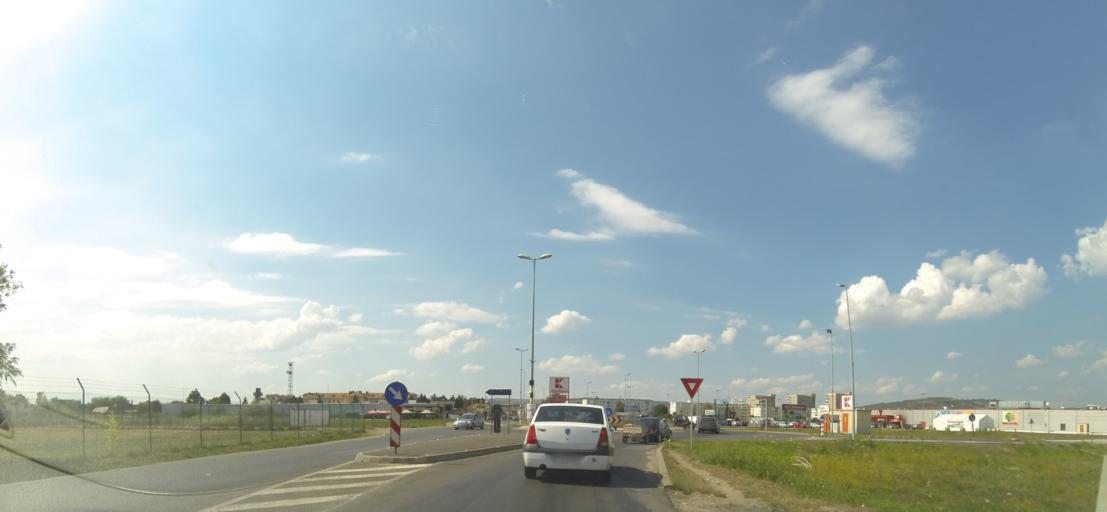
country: RO
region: Brasov
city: Fogarasch
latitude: 45.8396
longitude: 24.9893
